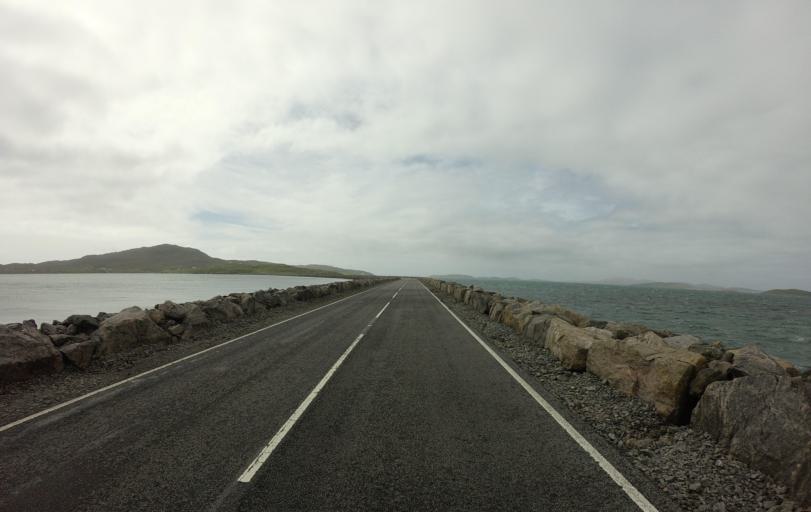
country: GB
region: Scotland
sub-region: Eilean Siar
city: Isle of South Uist
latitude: 57.0967
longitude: -7.3176
